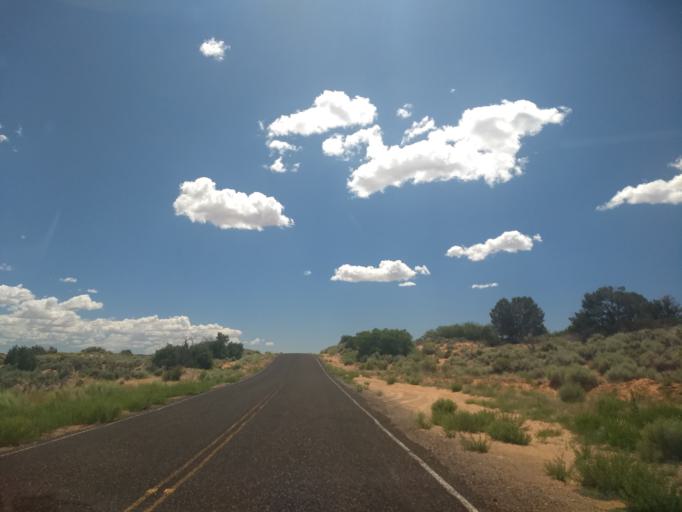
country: US
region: Utah
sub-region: Kane County
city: Kanab
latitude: 37.0423
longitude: -112.7264
